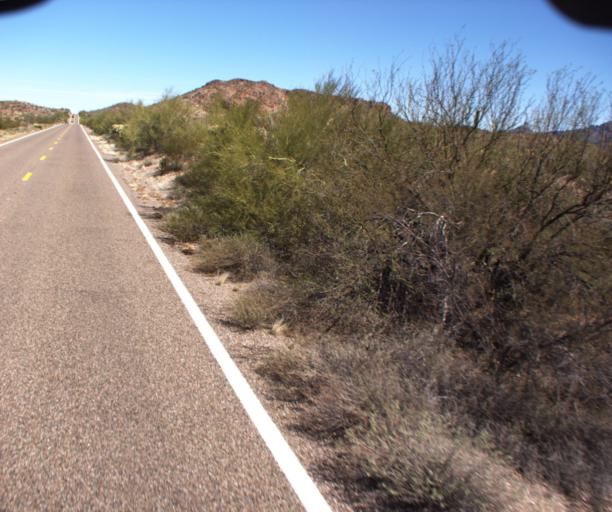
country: MX
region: Sonora
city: Sonoyta
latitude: 32.0769
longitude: -112.7806
